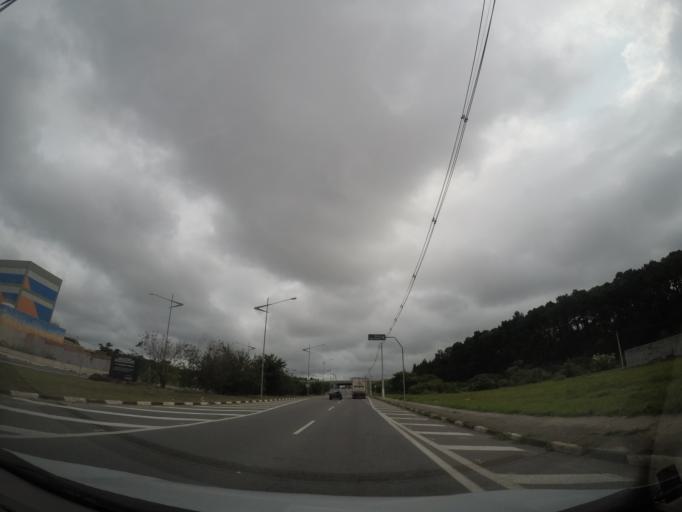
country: BR
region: Sao Paulo
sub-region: Aruja
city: Aruja
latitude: -23.4001
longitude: -46.3321
